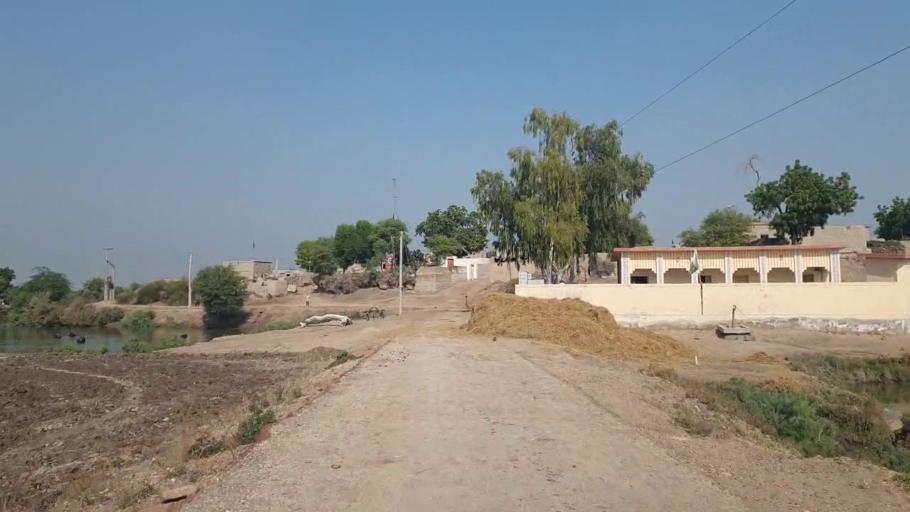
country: PK
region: Sindh
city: Sehwan
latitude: 26.4302
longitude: 67.7828
